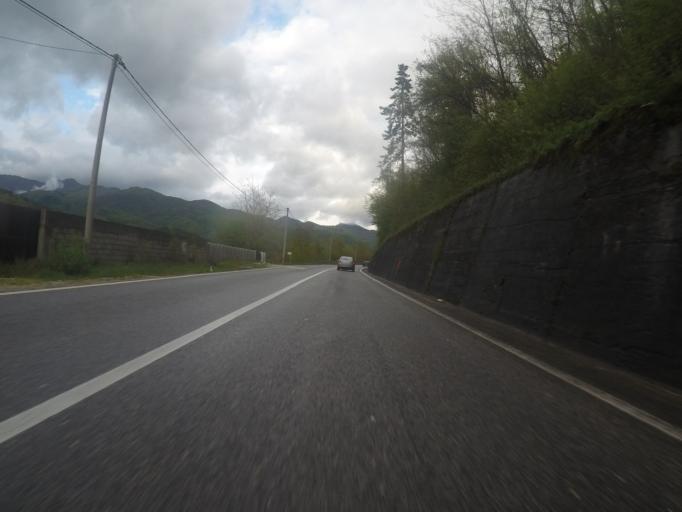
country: BA
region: Federation of Bosnia and Herzegovina
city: Jablanica
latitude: 43.6929
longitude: 17.8559
